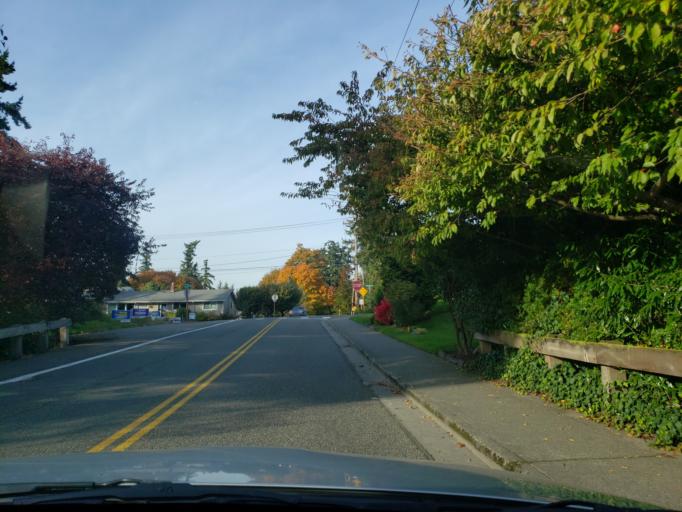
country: US
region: Washington
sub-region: Snohomish County
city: Mukilteo
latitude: 47.9379
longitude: -122.3012
